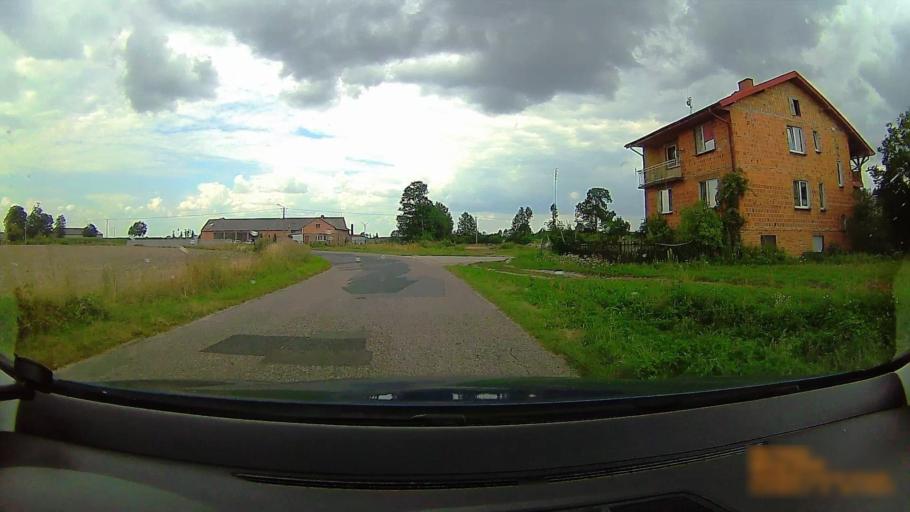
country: PL
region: Greater Poland Voivodeship
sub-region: Powiat koninski
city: Rychwal
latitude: 52.1064
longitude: 18.1897
